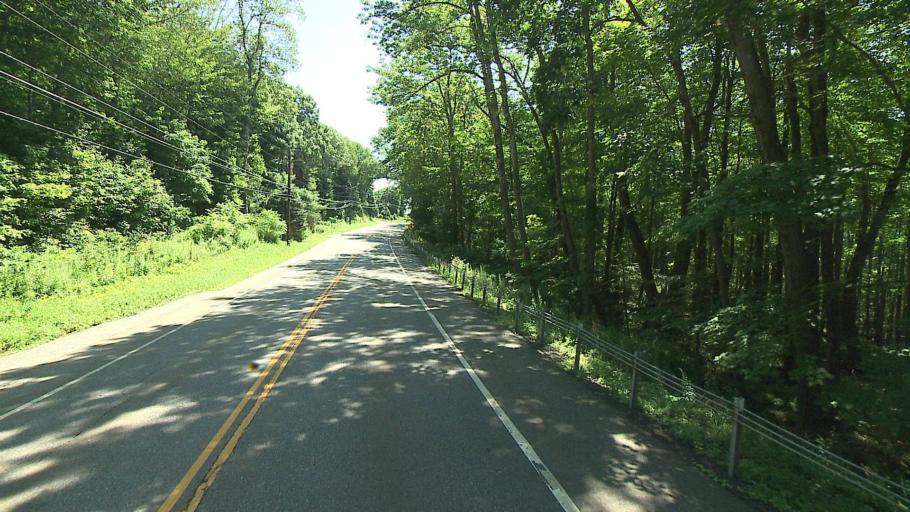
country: US
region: Connecticut
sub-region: Litchfield County
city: Litchfield
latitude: 41.8450
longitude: -73.2841
